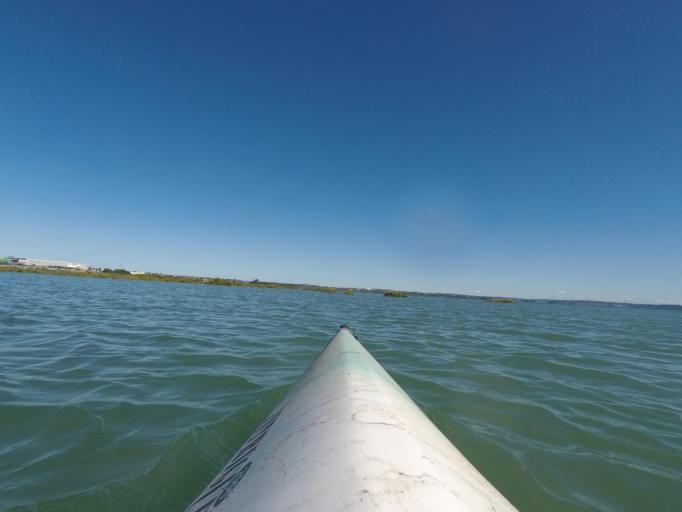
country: NZ
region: Auckland
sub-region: Auckland
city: Rosebank
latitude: -36.8696
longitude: 174.6799
